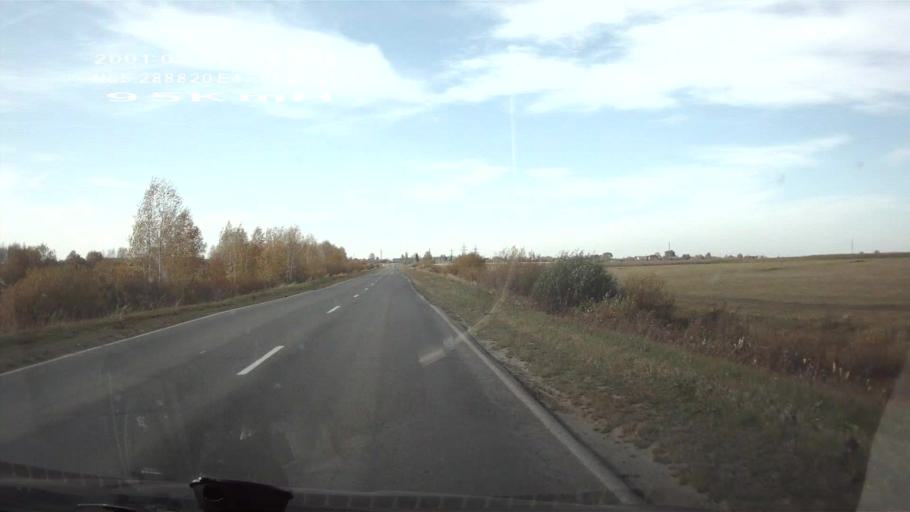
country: RU
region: Chuvashia
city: Ibresi
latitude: 55.2889
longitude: 47.0682
